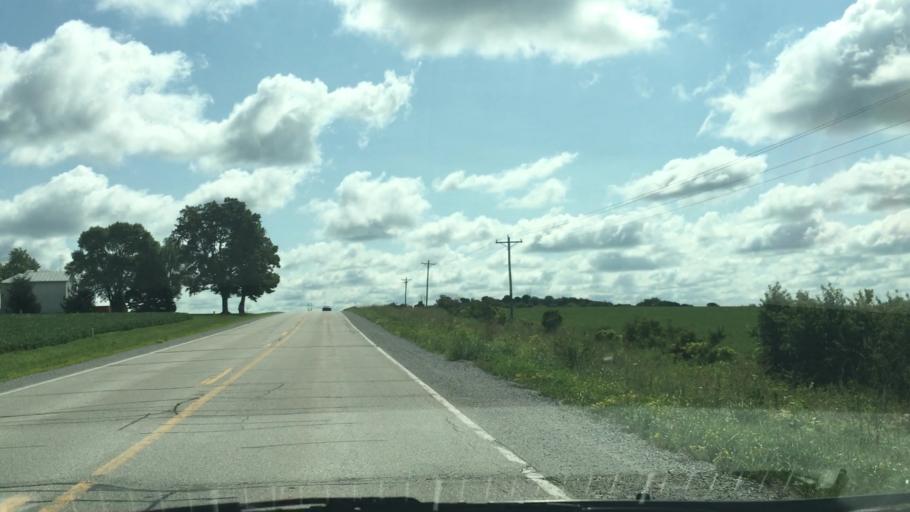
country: US
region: Iowa
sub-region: Johnson County
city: Solon
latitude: 41.8313
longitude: -91.4950
